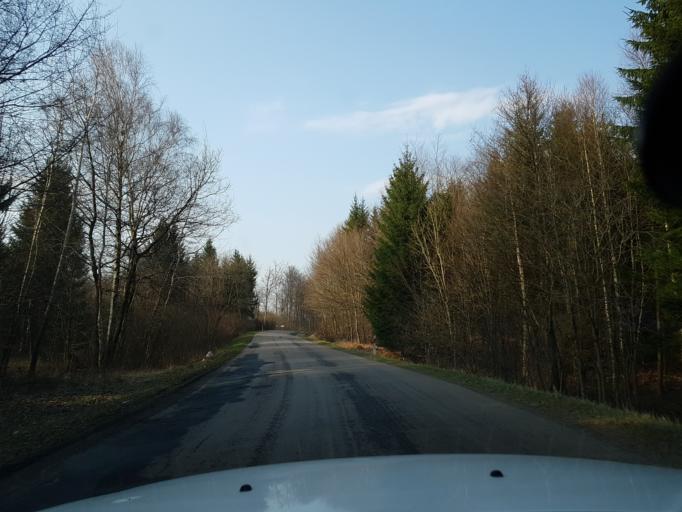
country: PL
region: West Pomeranian Voivodeship
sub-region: Powiat swidwinski
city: Polczyn-Zdroj
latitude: 53.7318
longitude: 16.0755
